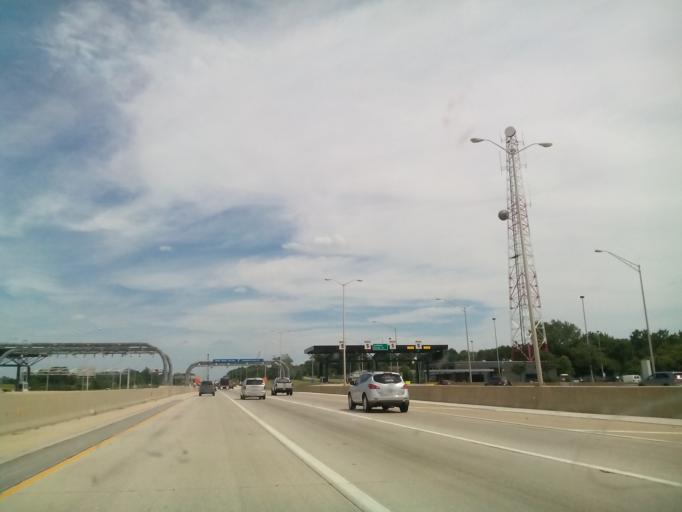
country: US
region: Illinois
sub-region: Kane County
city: North Aurora
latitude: 41.7967
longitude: -88.3109
